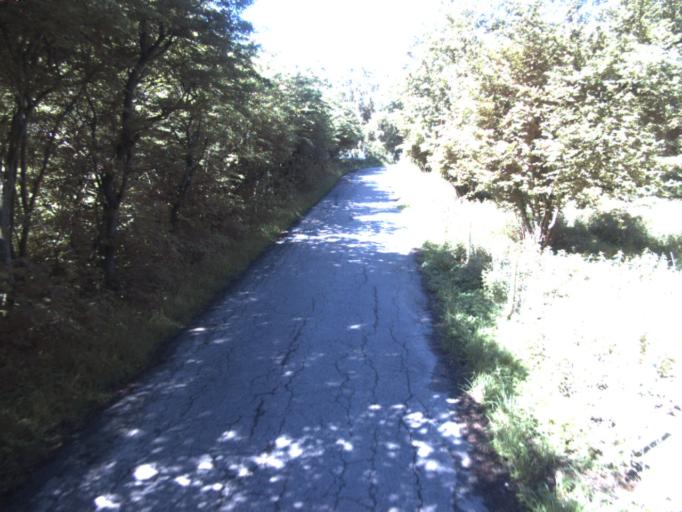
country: SE
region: Skane
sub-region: Helsingborg
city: Helsingborg
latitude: 56.0736
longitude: 12.6720
